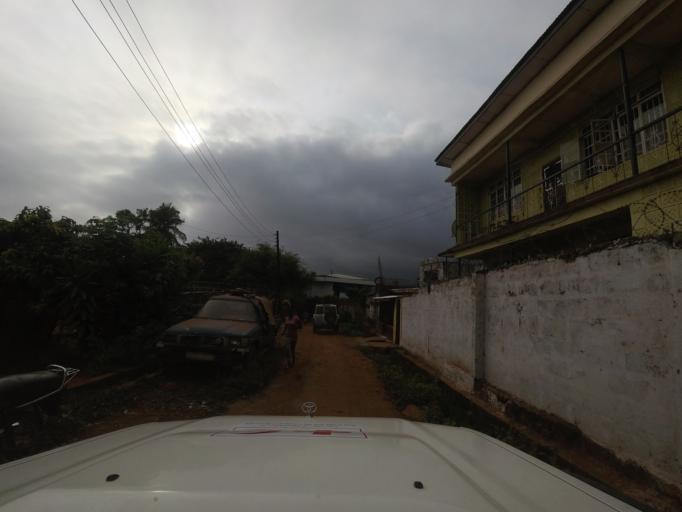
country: SL
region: Western Area
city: Freetown
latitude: 8.4859
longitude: -13.2619
